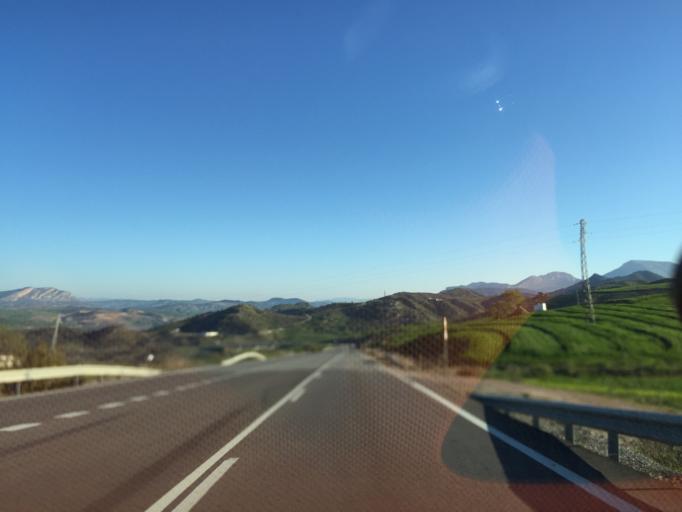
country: ES
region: Andalusia
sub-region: Provincia de Malaga
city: Ardales
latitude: 36.8686
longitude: -4.8412
